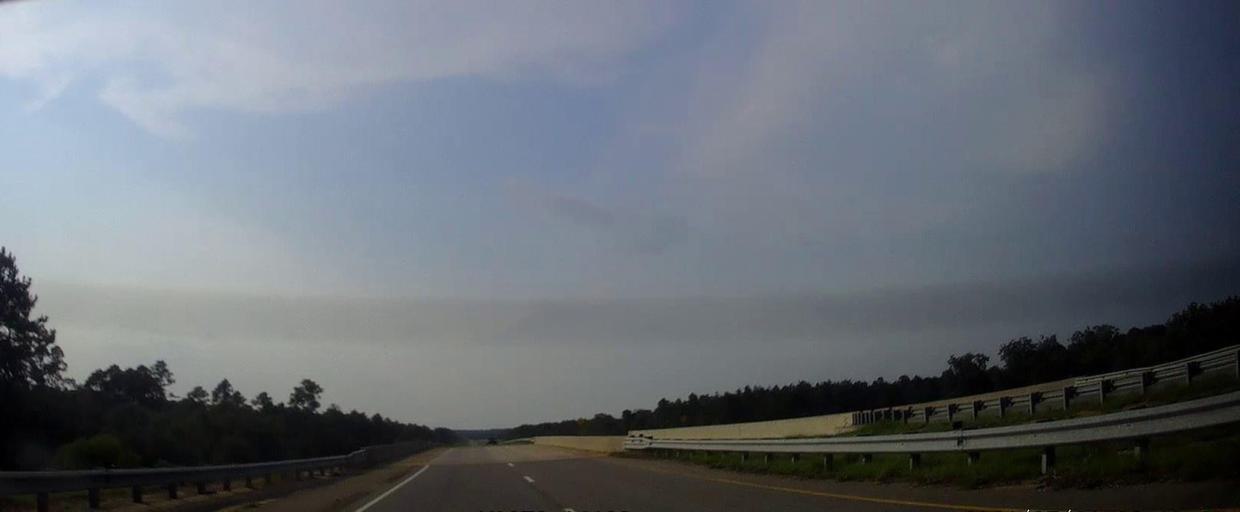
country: US
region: Georgia
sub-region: Laurens County
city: Dublin
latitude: 32.5225
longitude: -82.9626
